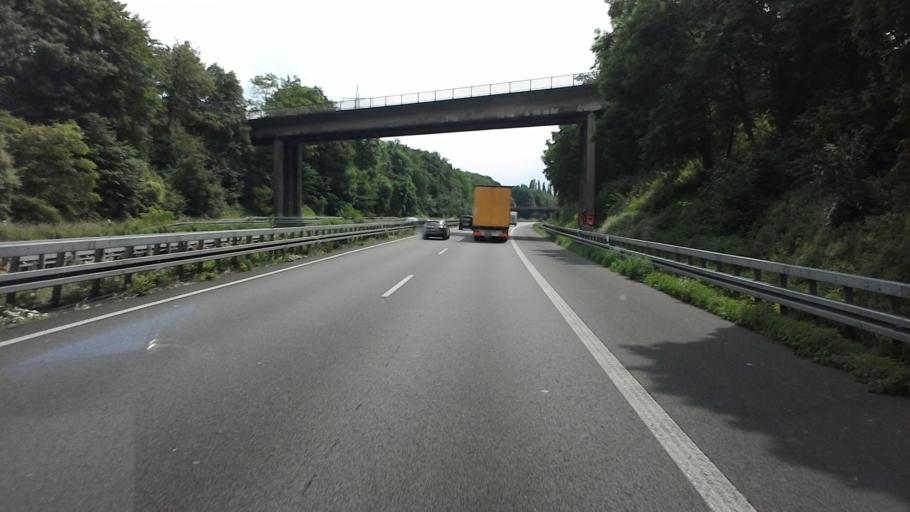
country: DE
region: North Rhine-Westphalia
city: Stolberg
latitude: 50.7817
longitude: 6.1767
